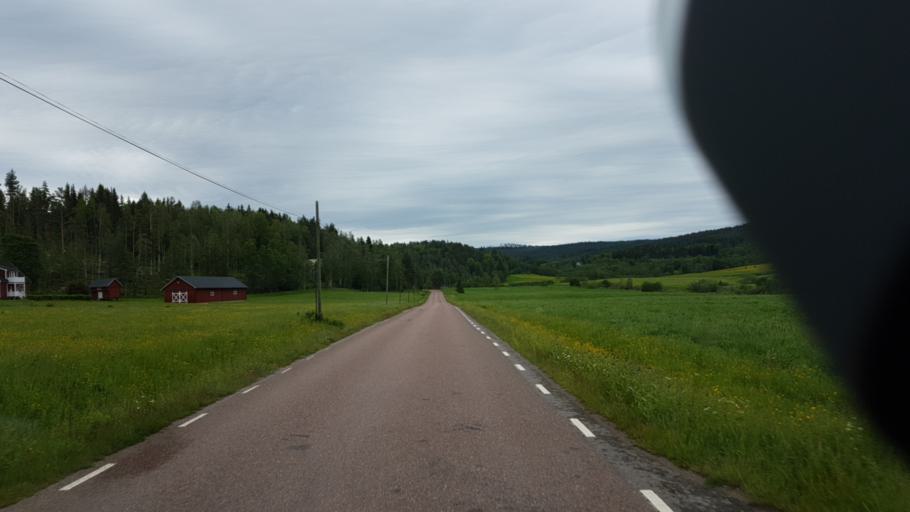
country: NO
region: Ostfold
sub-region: Romskog
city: Romskog
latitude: 59.7069
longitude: 12.0757
